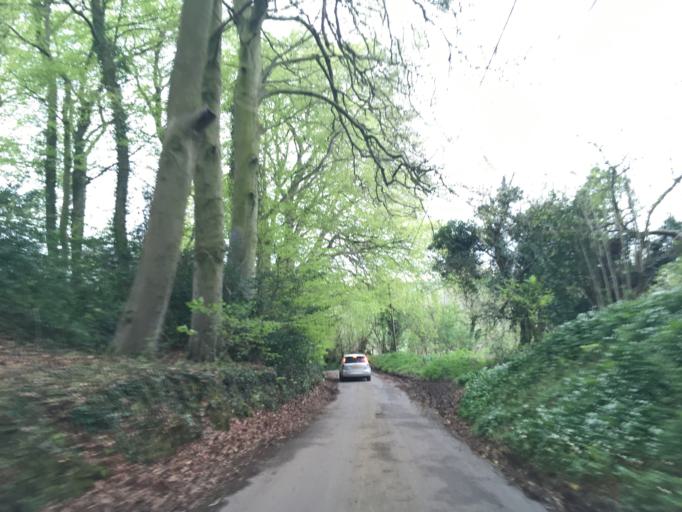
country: GB
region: England
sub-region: Gloucestershire
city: Wotton-under-Edge
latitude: 51.6402
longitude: -2.3328
